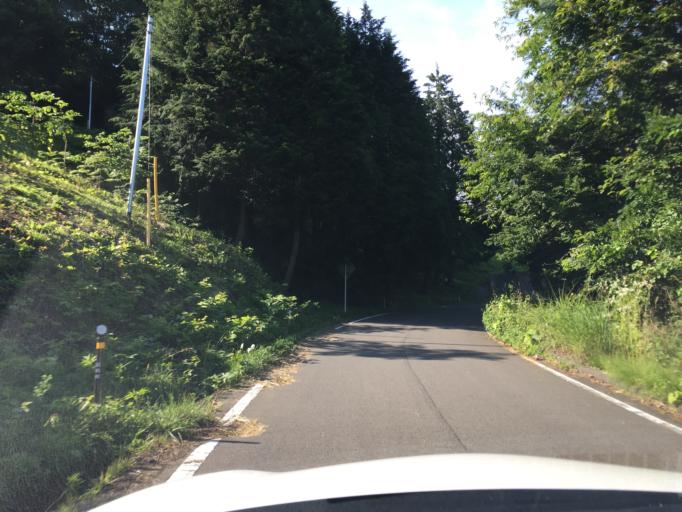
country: JP
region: Fukushima
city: Ishikawa
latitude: 37.2522
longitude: 140.4965
